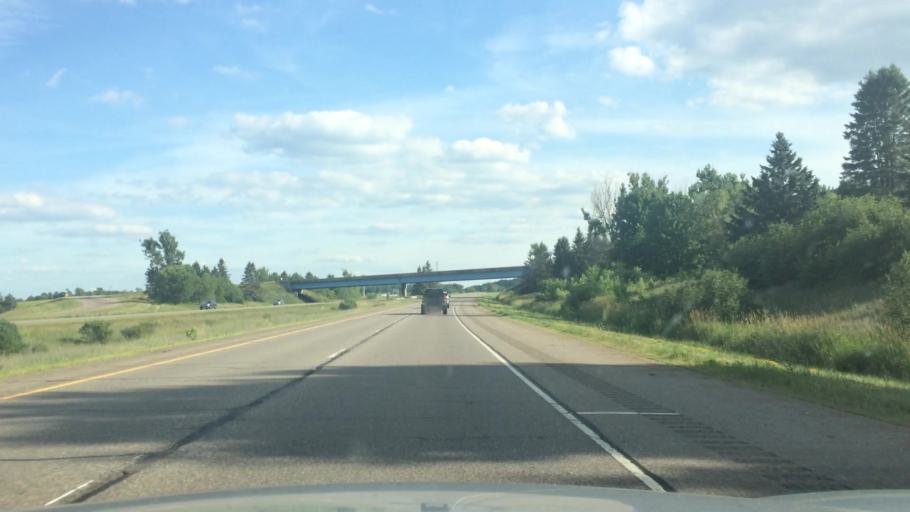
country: US
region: Wisconsin
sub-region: Lincoln County
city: Merrill
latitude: 45.1348
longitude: -89.6405
